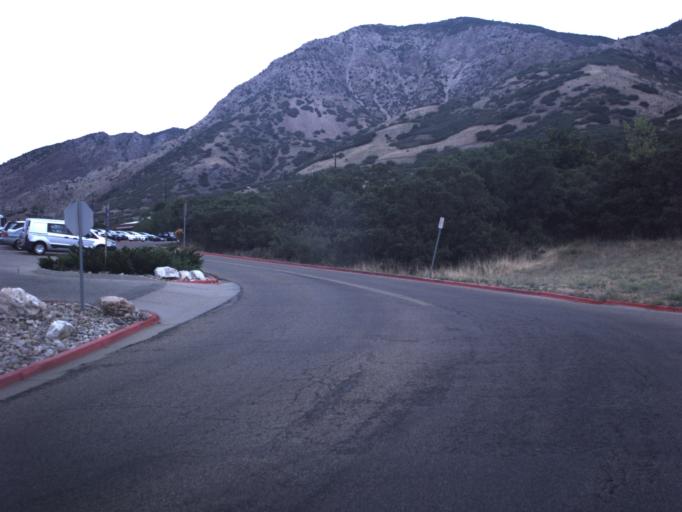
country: US
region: Utah
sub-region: Weber County
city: South Ogden
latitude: 41.1946
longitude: -111.9382
